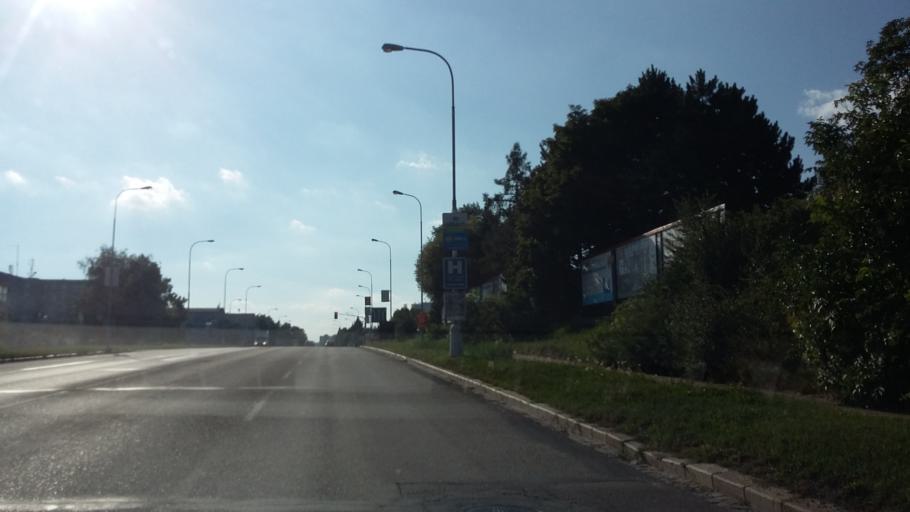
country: CZ
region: South Moravian
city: Moravany
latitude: 49.1731
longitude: 16.5865
